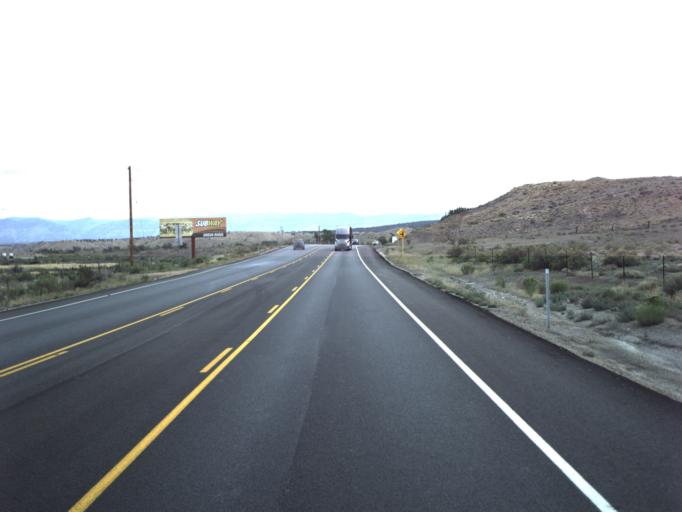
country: US
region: Utah
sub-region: Carbon County
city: Wellington
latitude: 39.5477
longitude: -110.6722
